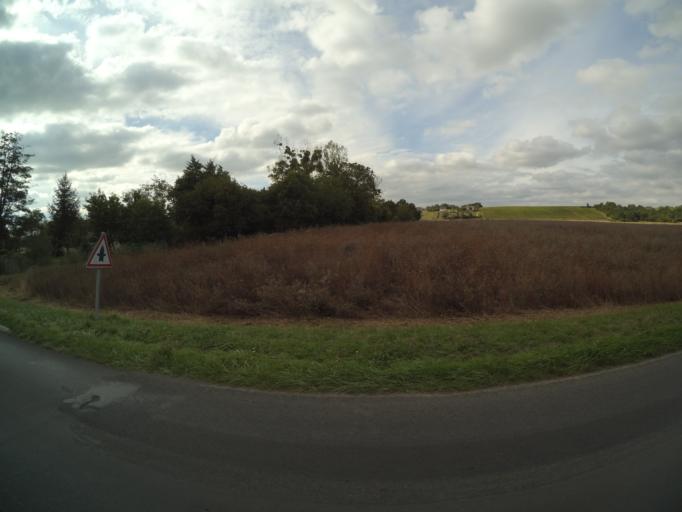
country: FR
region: Centre
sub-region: Departement d'Indre-et-Loire
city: Vernou-sur-Brenne
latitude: 47.4443
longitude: 0.8643
